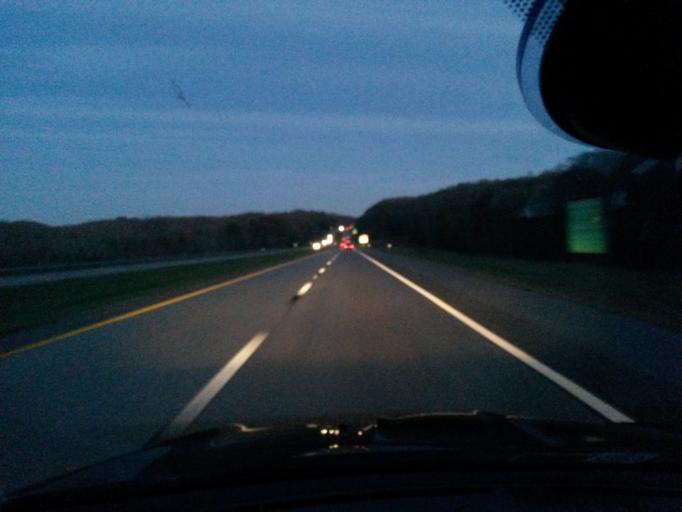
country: US
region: West Virginia
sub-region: Raleigh County
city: Shady Spring
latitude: 37.7663
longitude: -81.0178
